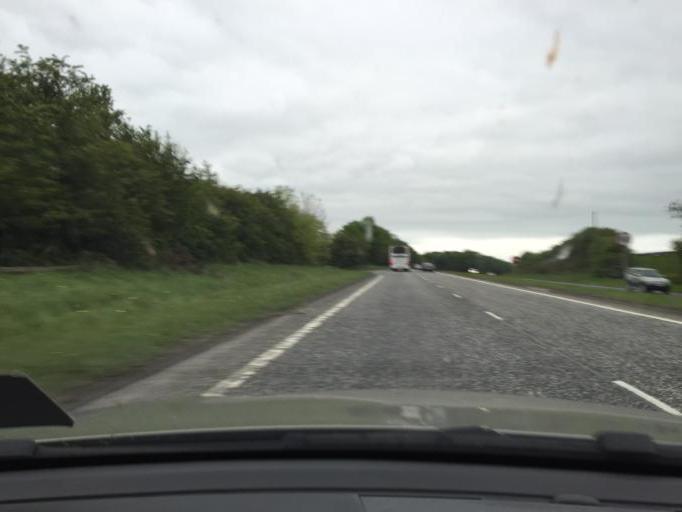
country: GB
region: Northern Ireland
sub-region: Banbridge District
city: Banbridge
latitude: 54.3527
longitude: -6.2401
